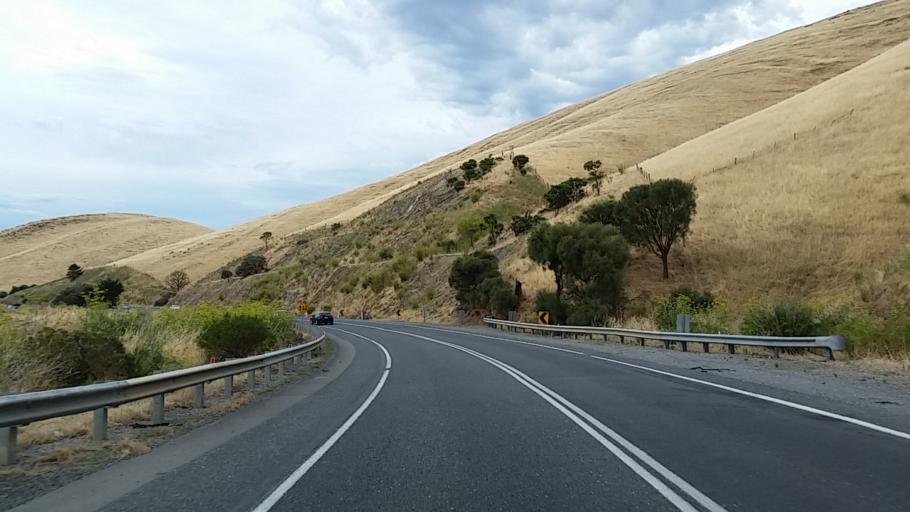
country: AU
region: South Australia
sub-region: Onkaparinga
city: Port Willunga
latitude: -35.3611
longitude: 138.4537
